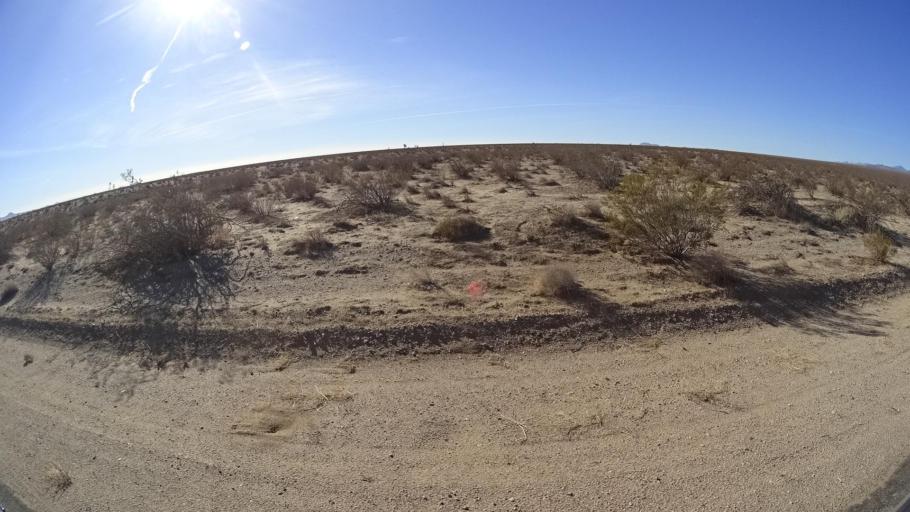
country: US
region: California
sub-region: Kern County
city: California City
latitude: 35.1985
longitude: -118.0606
